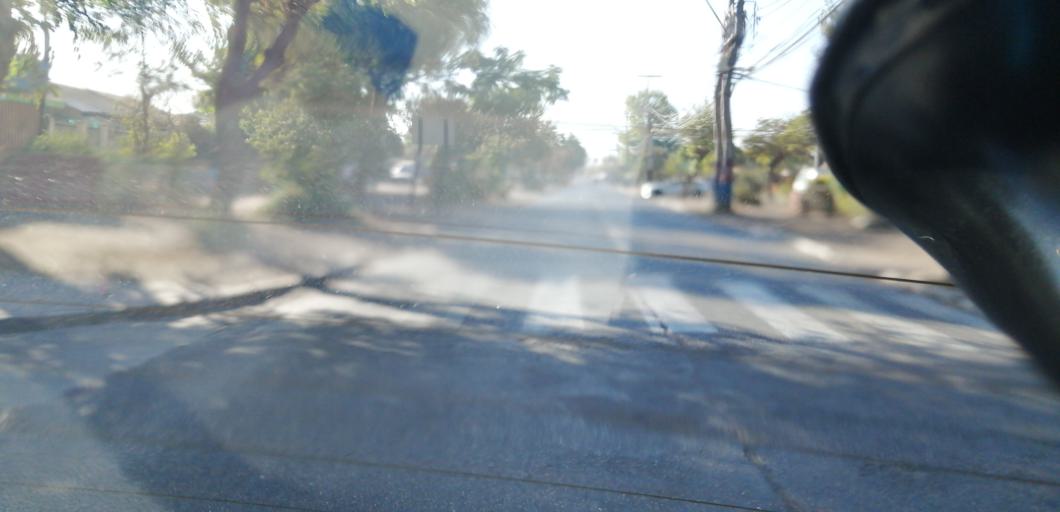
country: CL
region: Santiago Metropolitan
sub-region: Provincia de Santiago
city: Lo Prado
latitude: -33.4349
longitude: -70.7604
